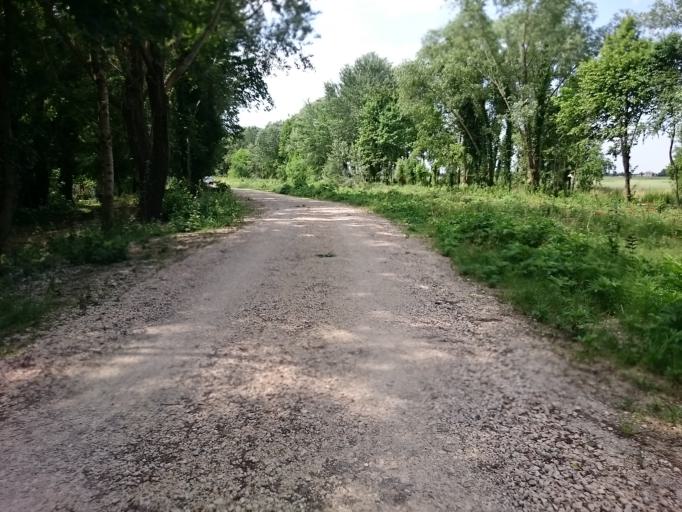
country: IT
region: Veneto
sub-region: Provincia di Padova
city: Este
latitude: 45.2196
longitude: 11.6537
